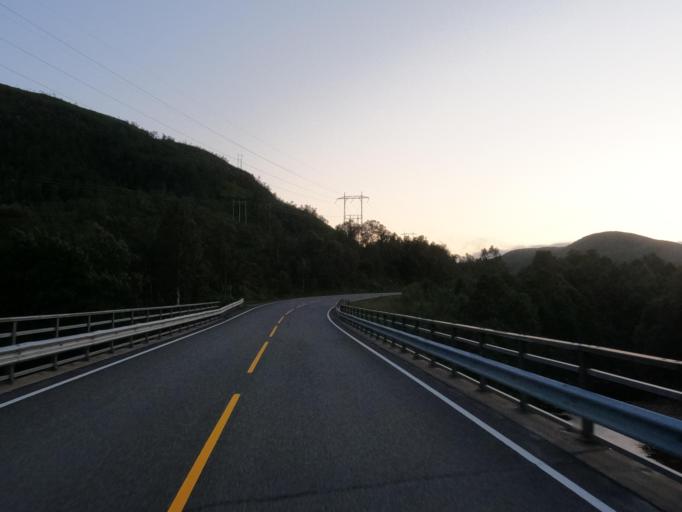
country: NO
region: Nordland
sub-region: Lodingen
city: Lodingen
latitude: 68.5170
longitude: 15.8684
